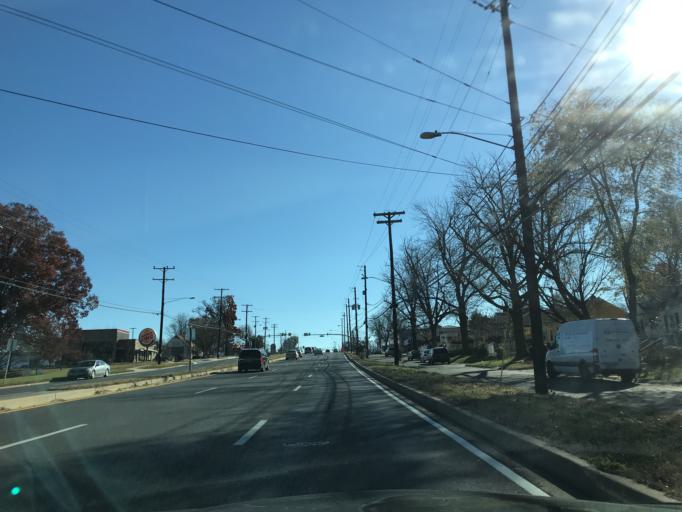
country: US
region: Maryland
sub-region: Montgomery County
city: Aspen Hill
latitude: 39.0582
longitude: -77.0863
